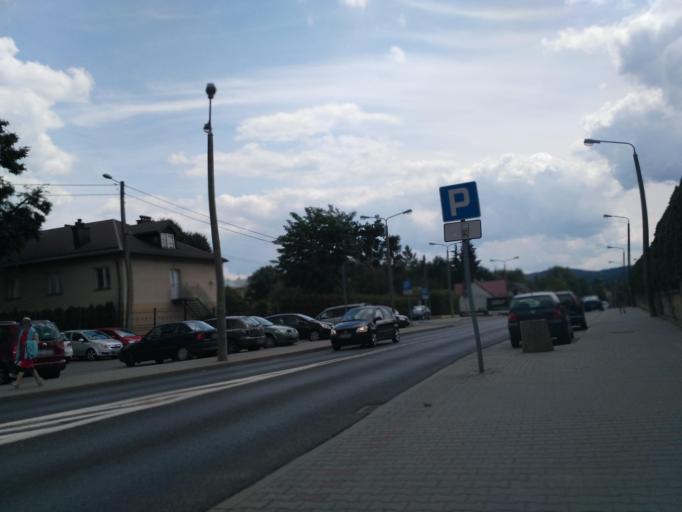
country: PL
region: Subcarpathian Voivodeship
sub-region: Powiat debicki
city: Debica
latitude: 50.0482
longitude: 21.4065
